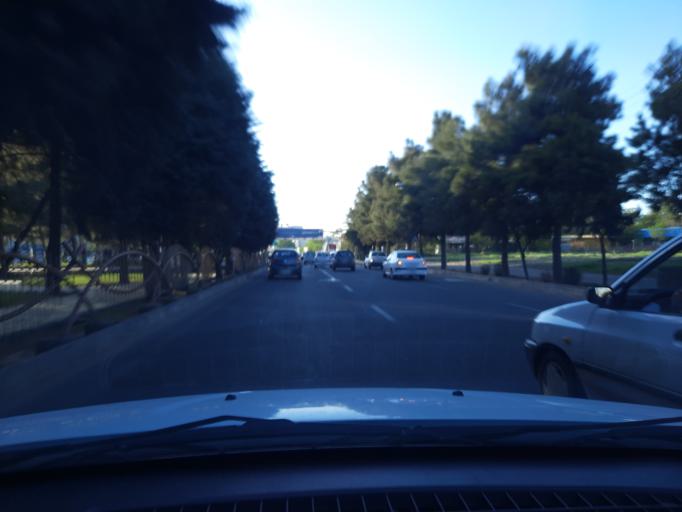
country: IR
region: Qazvin
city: Qazvin
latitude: 36.2817
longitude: 50.0224
